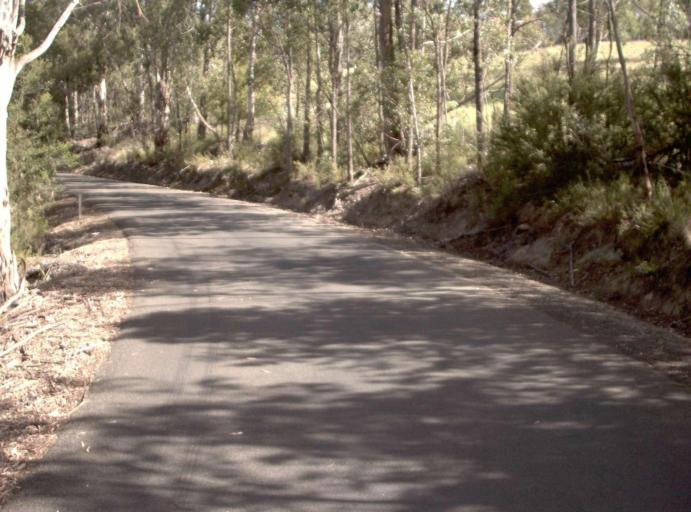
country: AU
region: Victoria
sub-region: East Gippsland
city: Lakes Entrance
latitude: -37.4745
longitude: 148.1256
